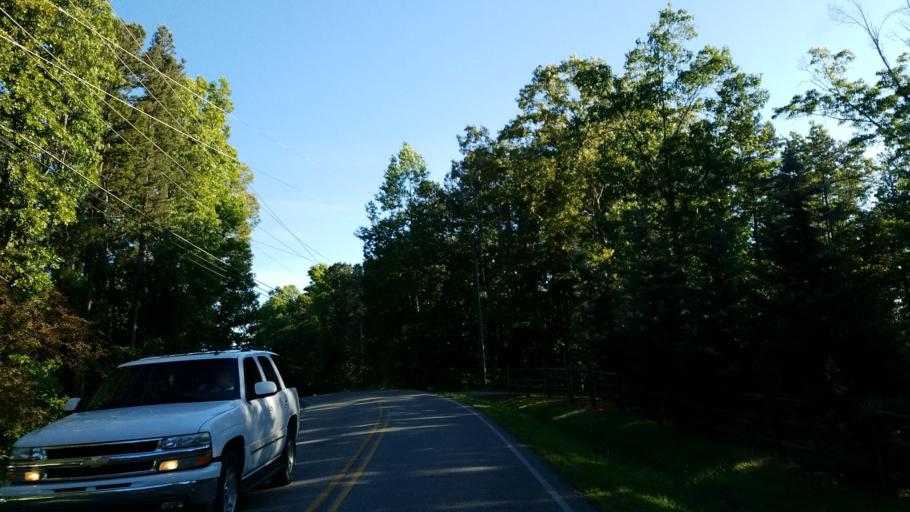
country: US
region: Georgia
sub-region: Cherokee County
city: Holly Springs
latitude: 34.1764
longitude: -84.5411
